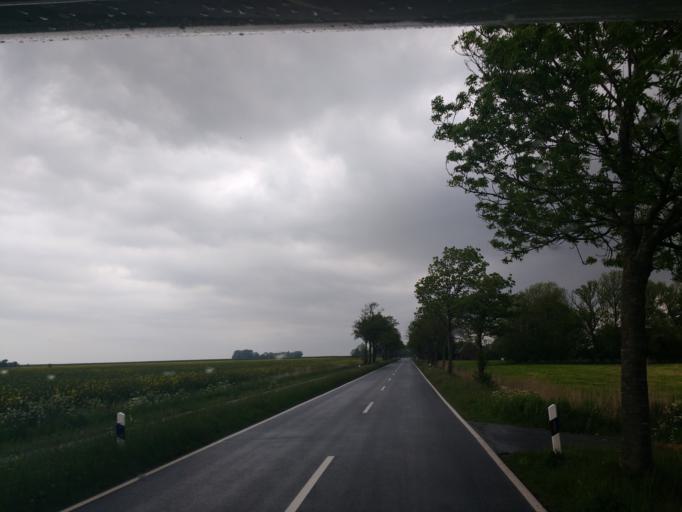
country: DE
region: Lower Saxony
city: Wangerooge
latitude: 53.6929
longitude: 7.9045
